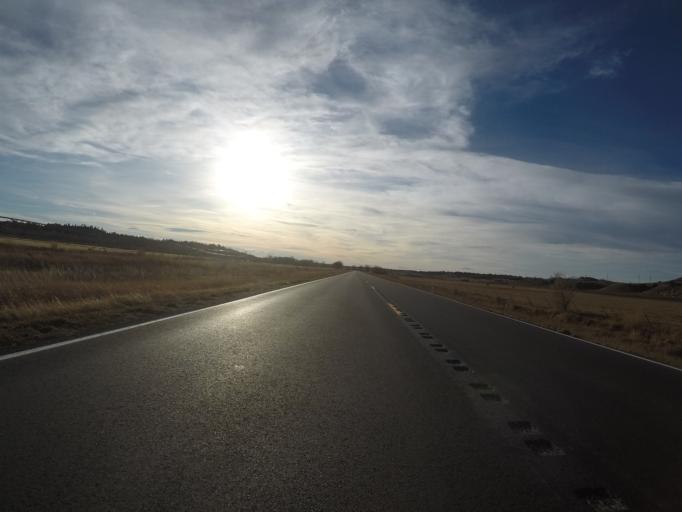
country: US
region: Montana
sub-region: Musselshell County
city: Roundup
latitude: 46.3650
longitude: -108.6545
